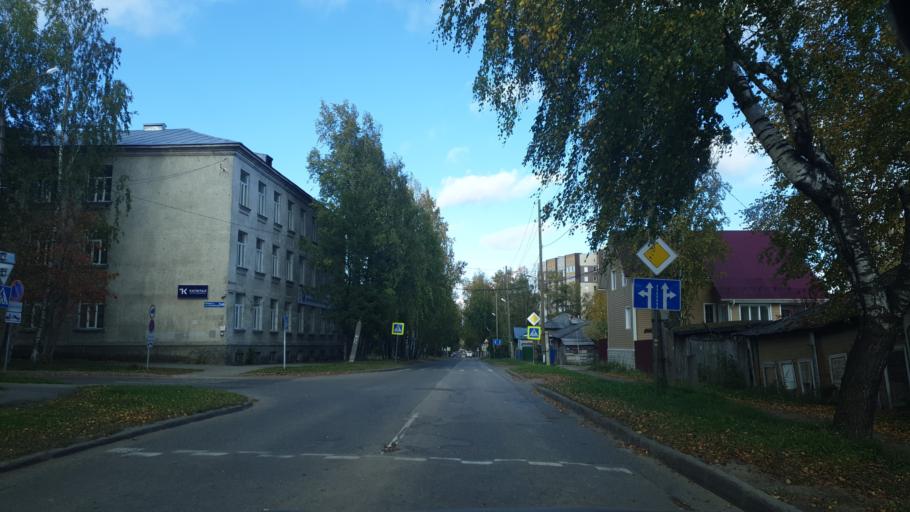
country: RU
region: Komi Republic
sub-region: Syktyvdinskiy Rayon
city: Syktyvkar
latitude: 61.6610
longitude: 50.8401
